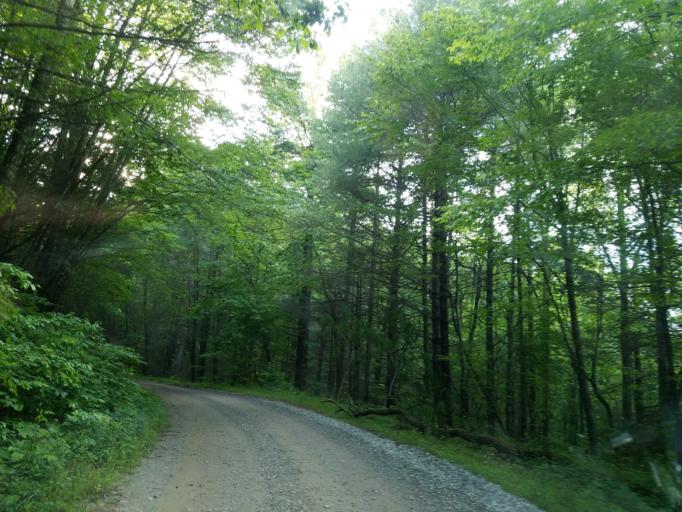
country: US
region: Georgia
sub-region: Union County
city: Blairsville
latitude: 34.7470
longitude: -84.0355
